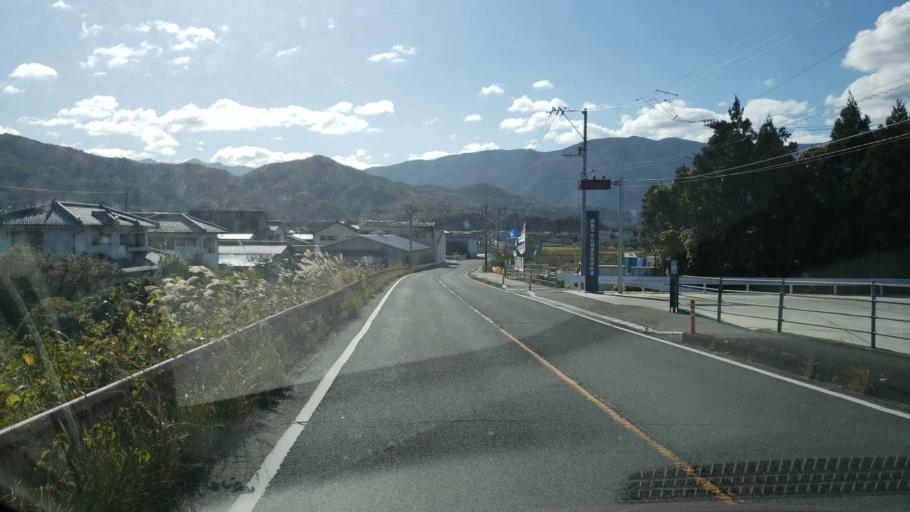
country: JP
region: Tokushima
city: Wakimachi
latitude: 34.0662
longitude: 134.2381
